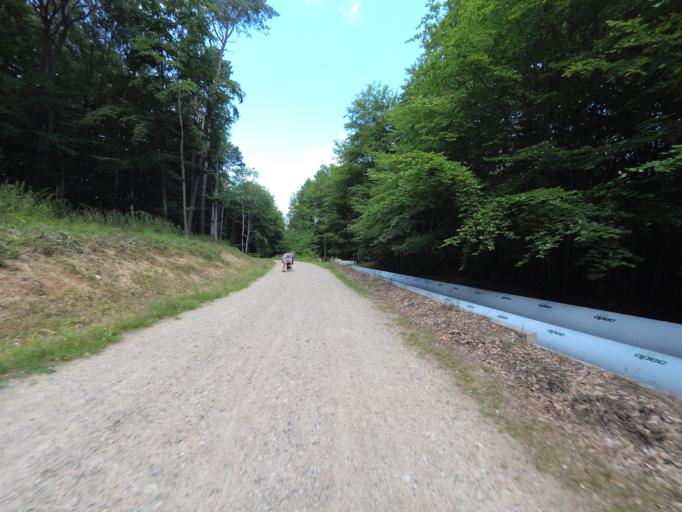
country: PL
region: Pomeranian Voivodeship
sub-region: Gdynia
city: Wielki Kack
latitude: 54.4806
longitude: 18.5015
